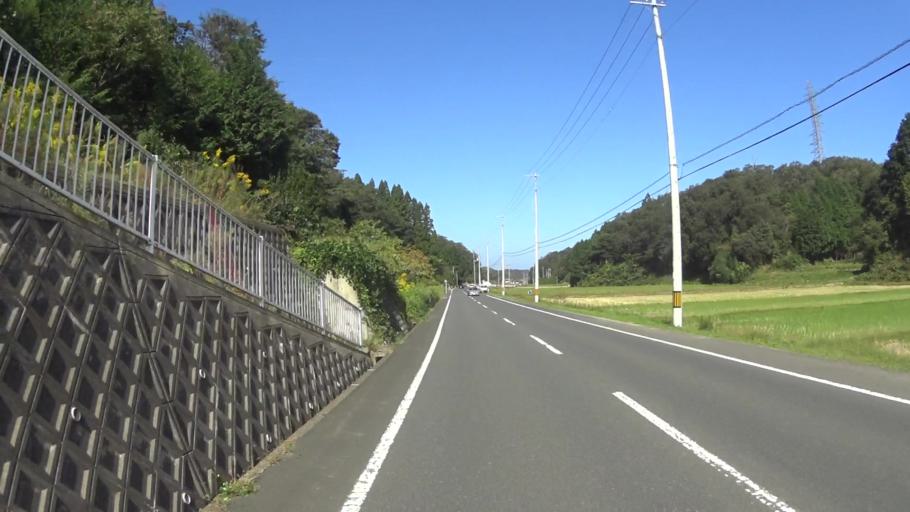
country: JP
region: Kyoto
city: Miyazu
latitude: 35.6666
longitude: 135.0598
